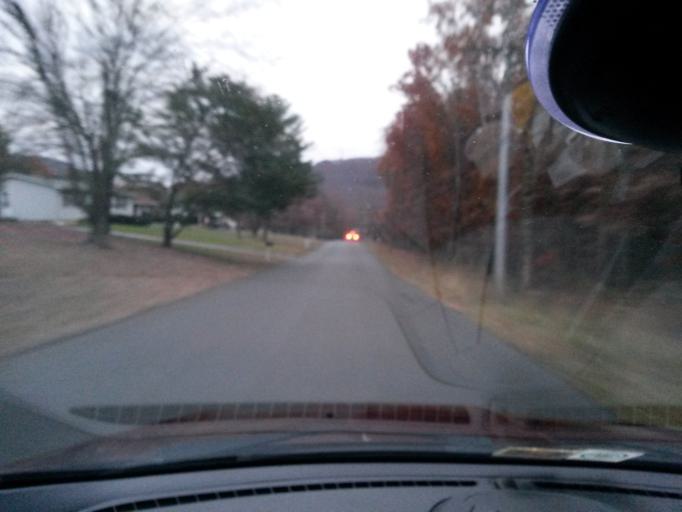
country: US
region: Virginia
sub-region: Alleghany County
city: Clifton Forge
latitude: 37.8215
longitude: -79.8125
